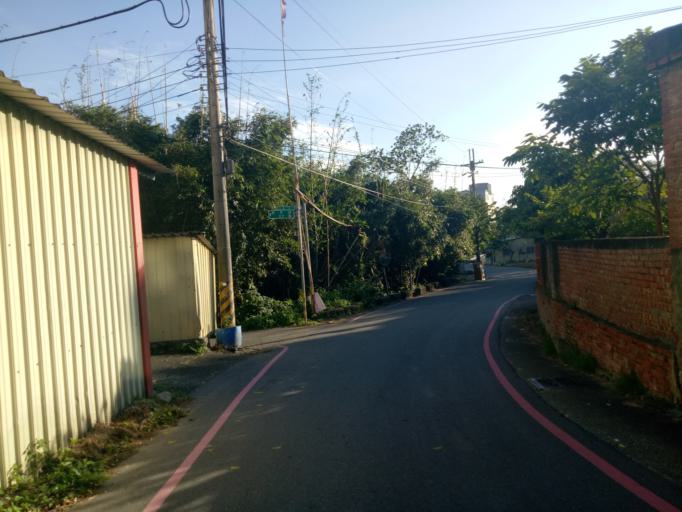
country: TW
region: Taiwan
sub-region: Hsinchu
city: Hsinchu
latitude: 24.7572
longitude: 120.9475
